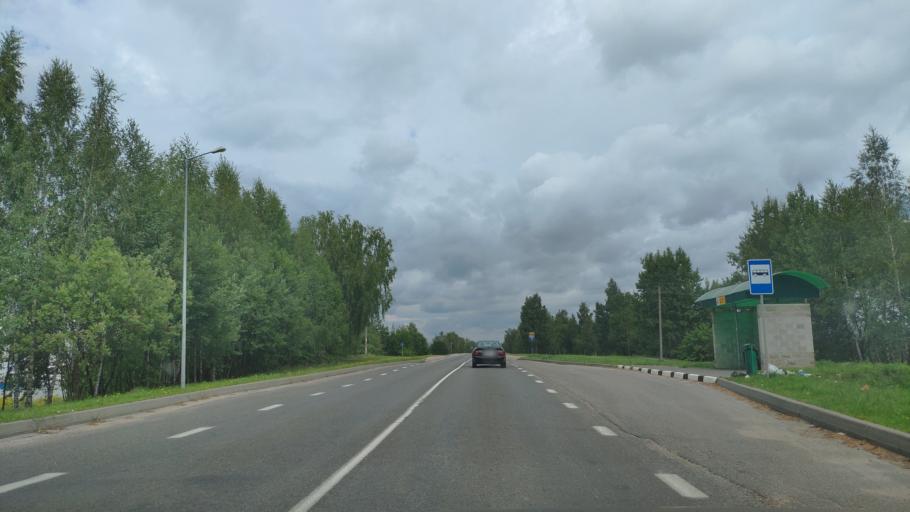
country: BY
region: Minsk
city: Zaslawye
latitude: 53.9899
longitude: 27.2621
